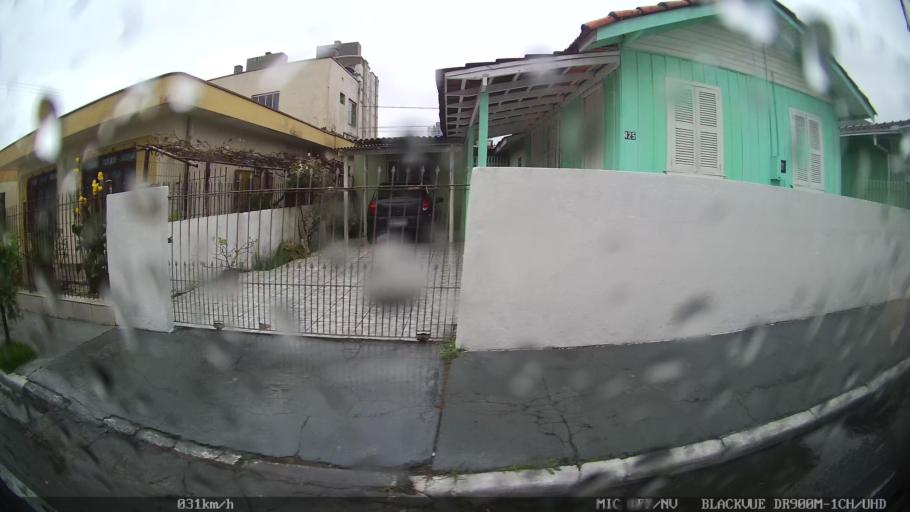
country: BR
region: Santa Catarina
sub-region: Itajai
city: Itajai
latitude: -26.8994
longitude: -48.6759
